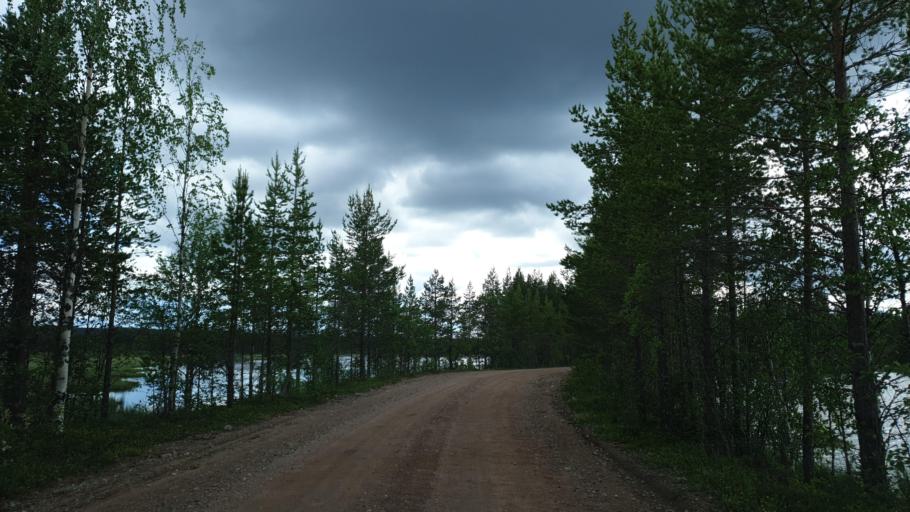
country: SE
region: Jaemtland
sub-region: Harjedalens Kommun
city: Sveg
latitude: 62.0347
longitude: 14.4934
